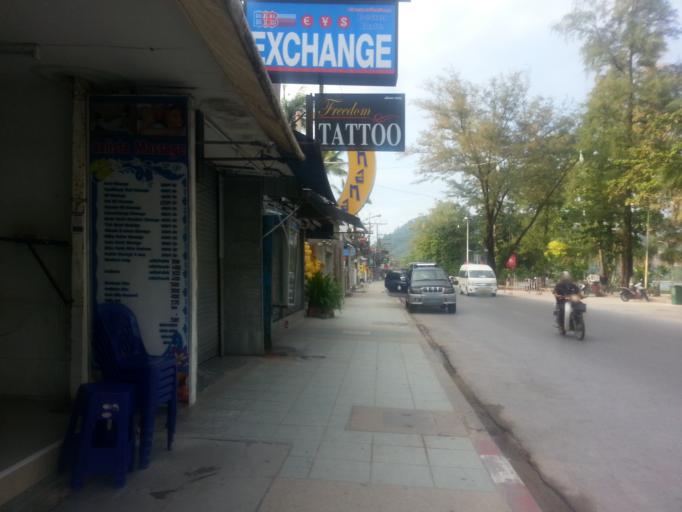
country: TH
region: Phuket
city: Patong
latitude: 7.8933
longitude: 98.2949
